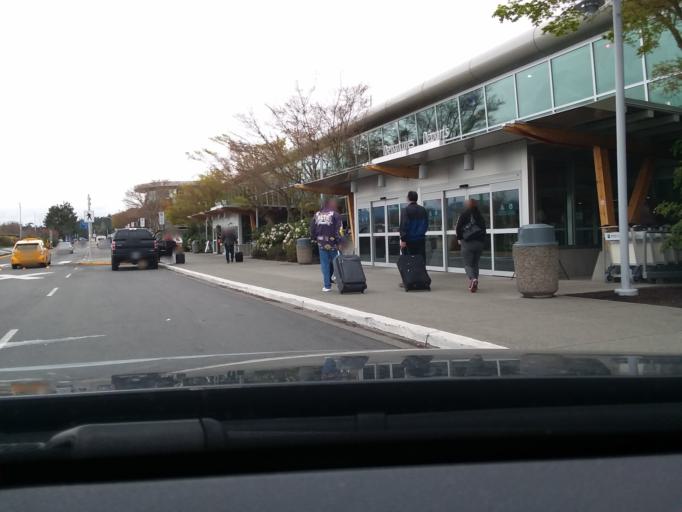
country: CA
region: British Columbia
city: North Saanich
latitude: 48.6401
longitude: -123.4291
